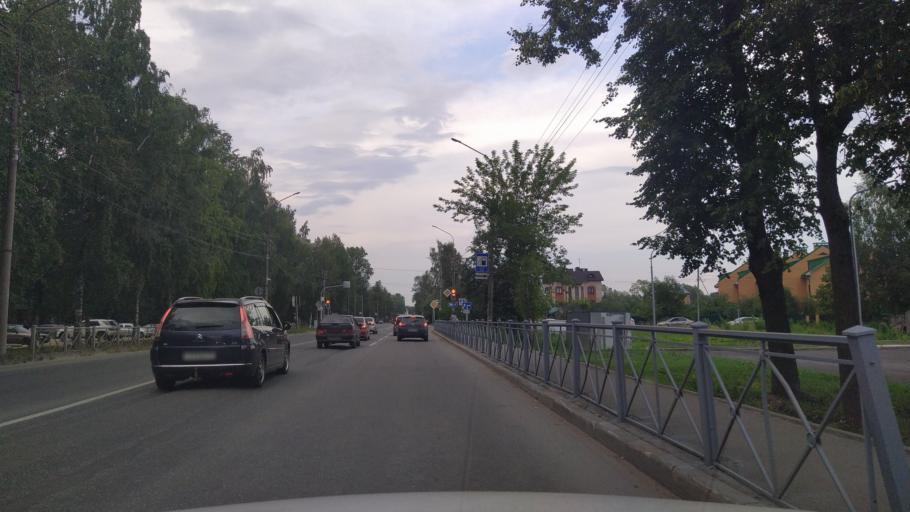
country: RU
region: Novgorod
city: Velikiy Novgorod
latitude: 58.5182
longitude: 31.2497
